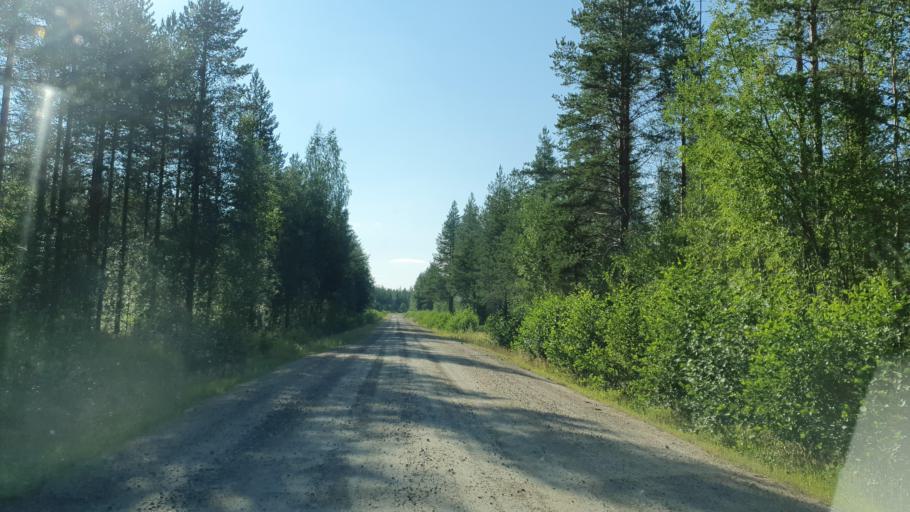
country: FI
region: Kainuu
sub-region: Kehys-Kainuu
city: Kuhmo
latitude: 64.0279
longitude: 29.7080
